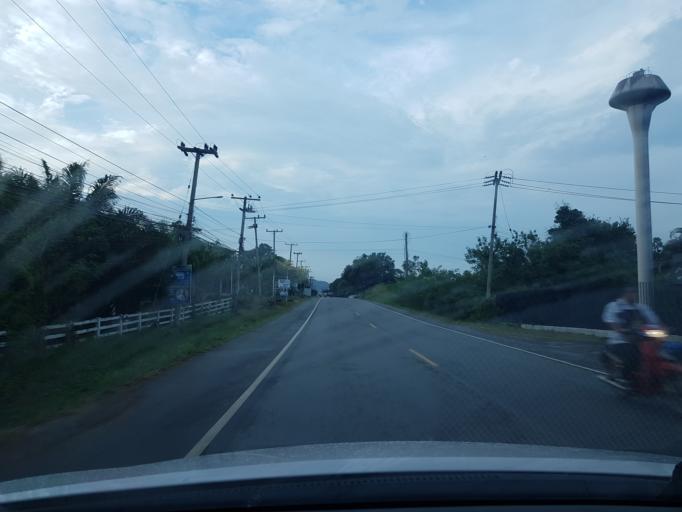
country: TH
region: Sara Buri
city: Muak Lek
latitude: 14.6078
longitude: 101.1969
